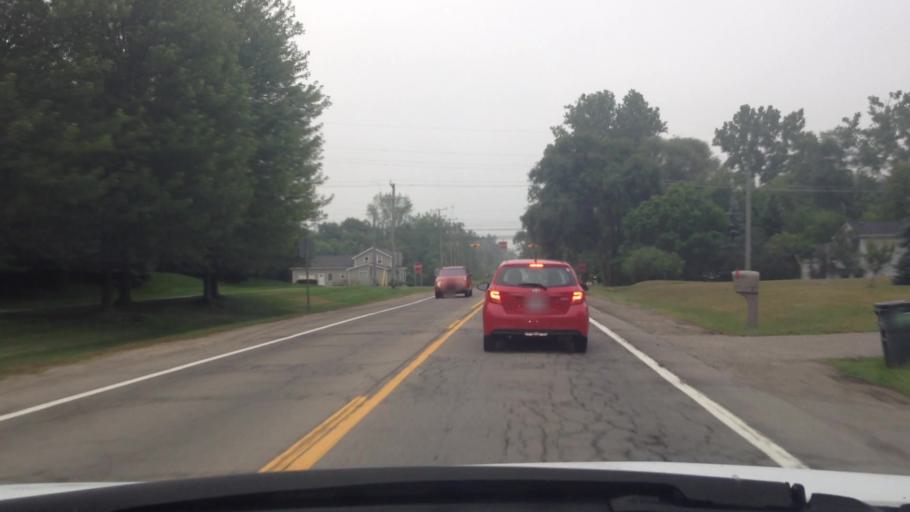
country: US
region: Michigan
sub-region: Oakland County
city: Clarkston
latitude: 42.7356
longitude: -83.3500
